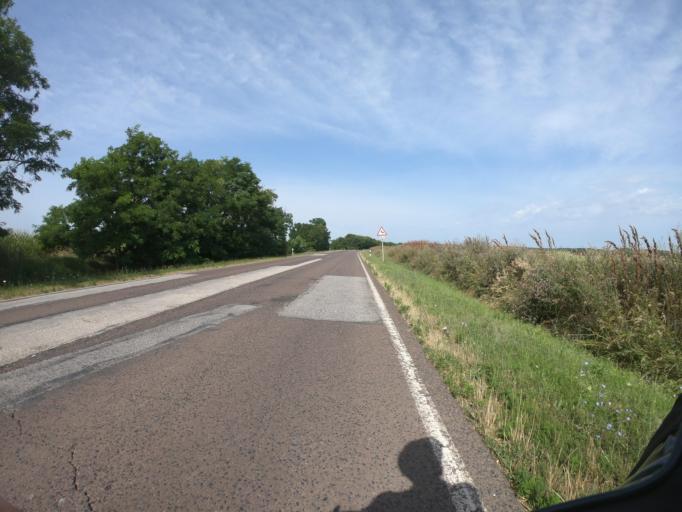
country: HU
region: Jasz-Nagykun-Szolnok
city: Tiszafured
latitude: 47.5947
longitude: 20.8312
